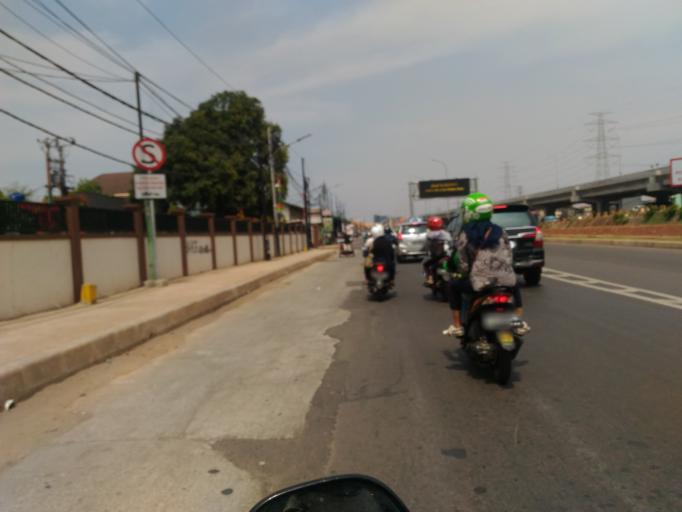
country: ID
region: Jakarta Raya
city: Jakarta
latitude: -6.2396
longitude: 106.8822
